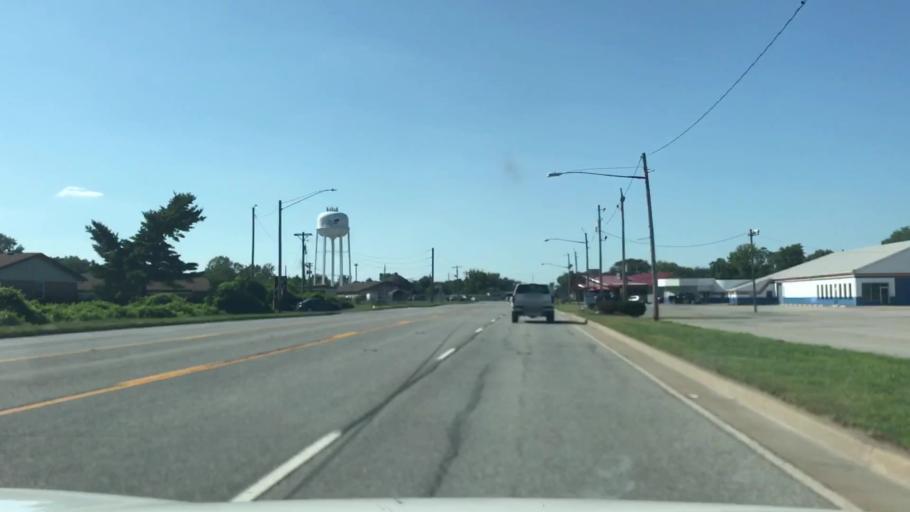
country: US
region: Illinois
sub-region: Madison County
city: Roxana
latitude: 38.8593
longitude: -90.0702
